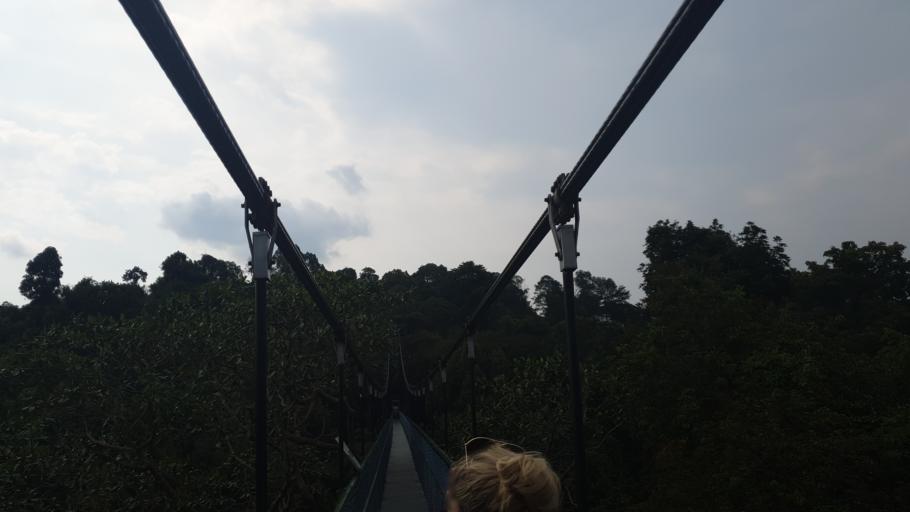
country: SG
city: Singapore
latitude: 1.3610
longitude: 103.8117
